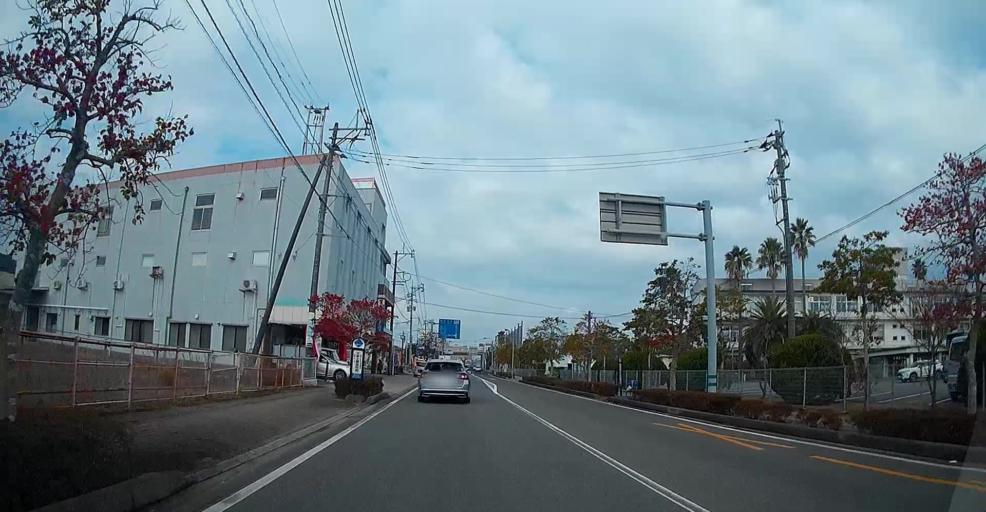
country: JP
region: Kumamoto
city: Hondo
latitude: 32.4457
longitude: 130.2020
